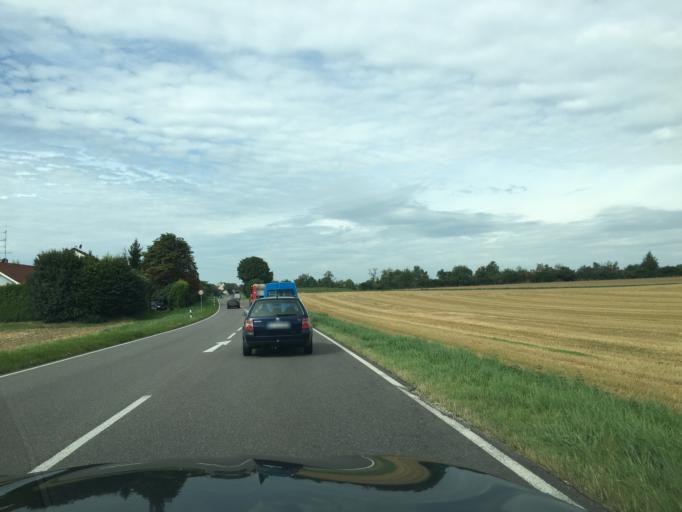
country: DE
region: Baden-Wuerttemberg
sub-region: Tuebingen Region
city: Opfingen
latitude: 48.2889
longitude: 9.7862
